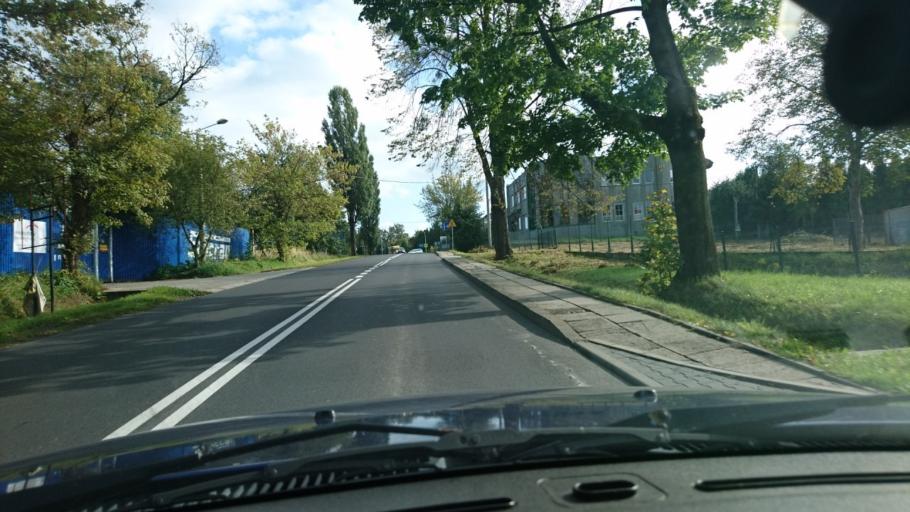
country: PL
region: Silesian Voivodeship
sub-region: Bielsko-Biala
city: Bielsko-Biala
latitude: 49.8620
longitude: 19.0315
